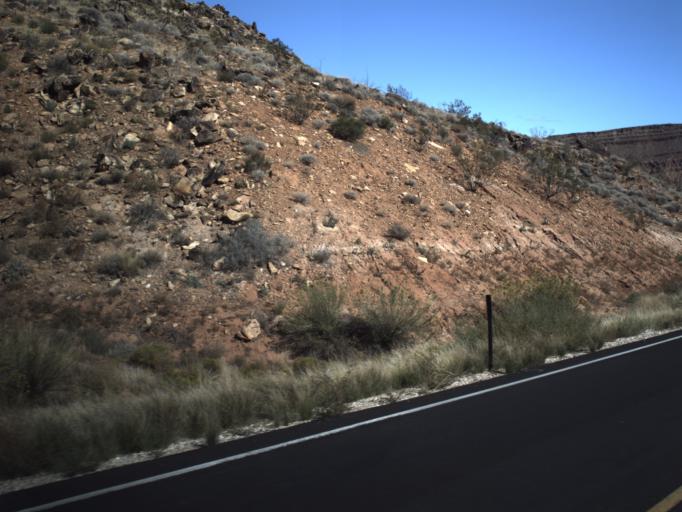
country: US
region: Utah
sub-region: Washington County
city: Hurricane
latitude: 37.1889
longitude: -113.3939
